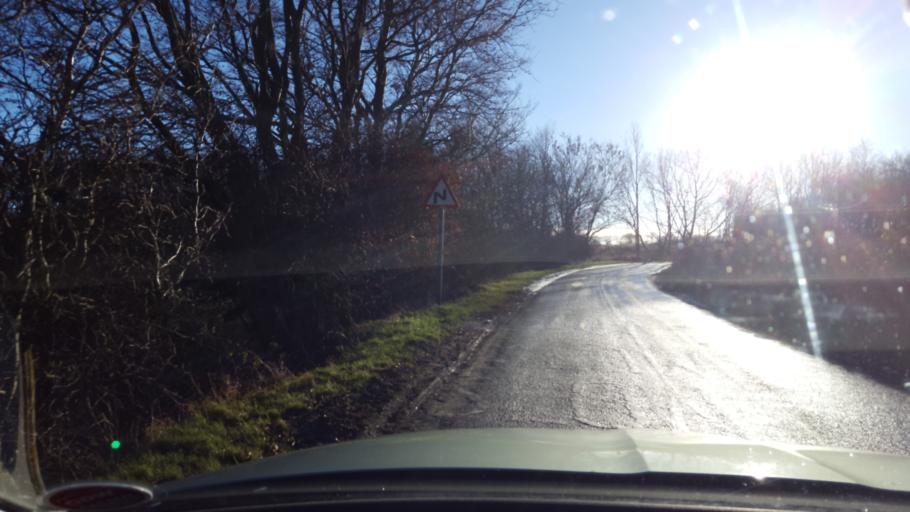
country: GB
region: Scotland
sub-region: West Lothian
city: Livingston
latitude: 55.9600
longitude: -3.5341
